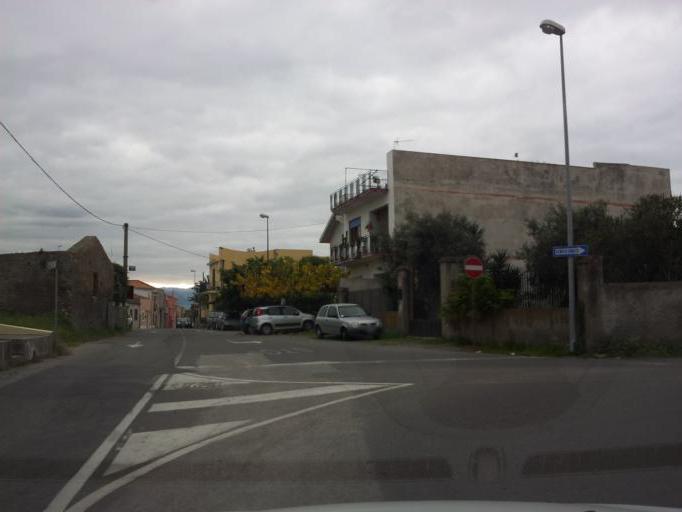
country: IT
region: Sicily
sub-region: Messina
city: Milazzo
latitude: 38.2497
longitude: 15.2470
